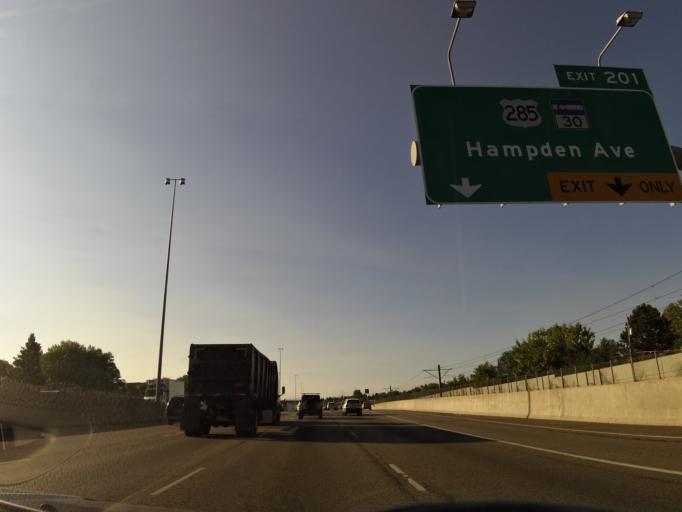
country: US
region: Colorado
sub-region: Arapahoe County
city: Cherry Hills Village
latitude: 39.6581
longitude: -104.9208
